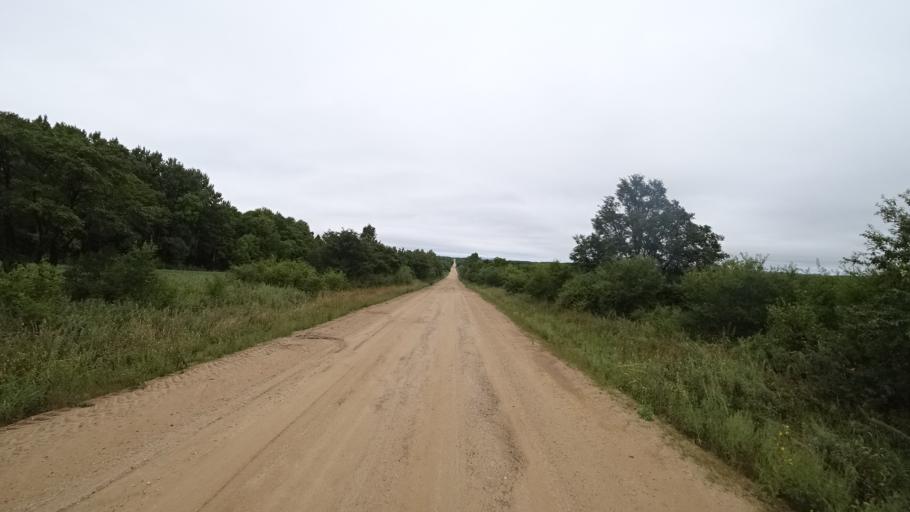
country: RU
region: Primorskiy
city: Ivanovka
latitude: 44.0622
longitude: 132.5686
